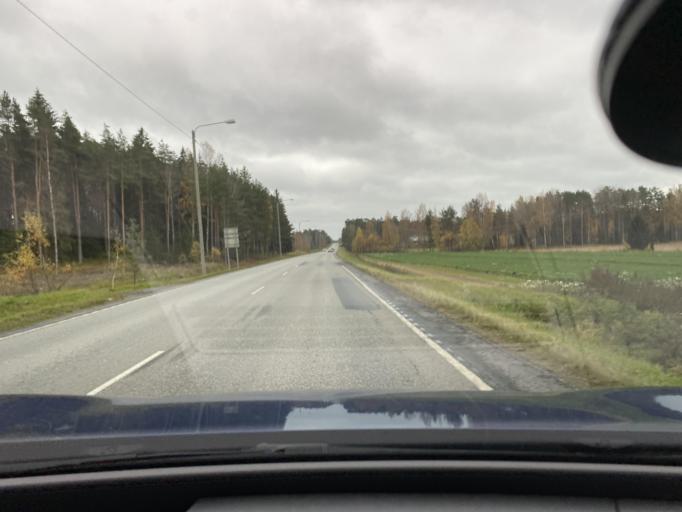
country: FI
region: Varsinais-Suomi
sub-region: Vakka-Suomi
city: Laitila
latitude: 60.9734
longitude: 21.5933
